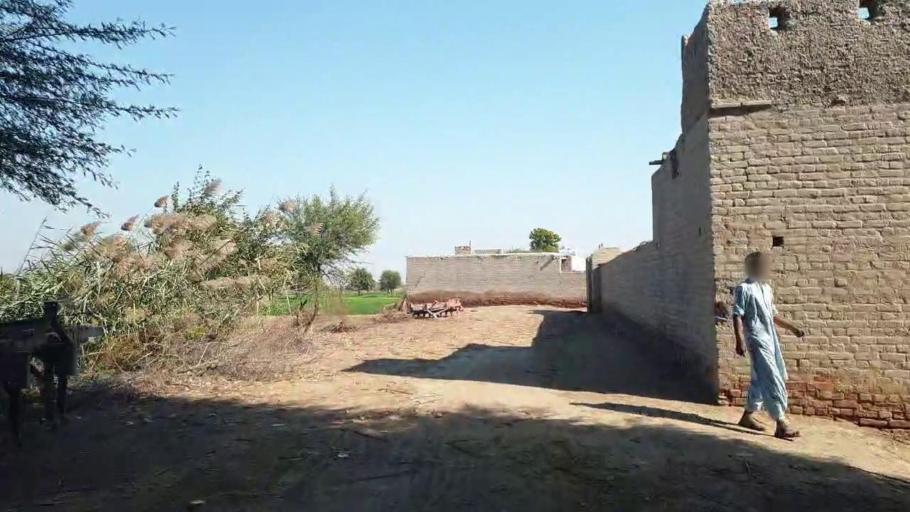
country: PK
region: Sindh
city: Shahdadpur
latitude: 25.9625
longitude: 68.6522
